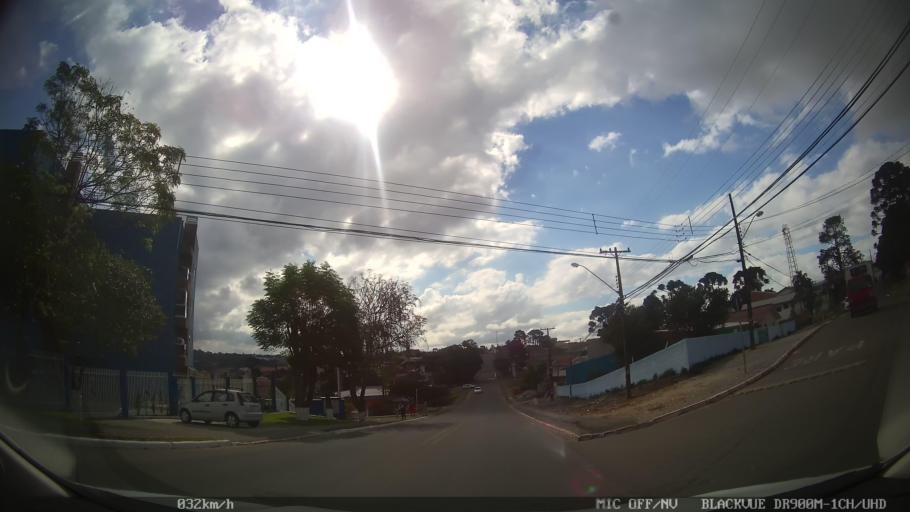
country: BR
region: Parana
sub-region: Colombo
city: Colombo
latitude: -25.3632
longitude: -49.1908
